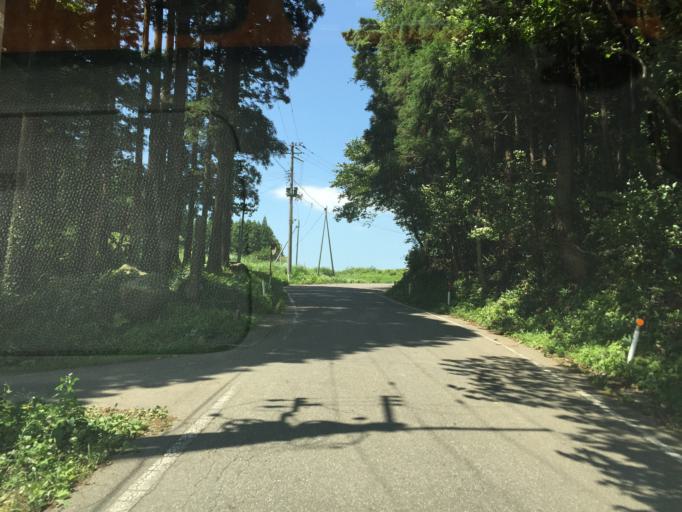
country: JP
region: Fukushima
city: Inawashiro
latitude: 37.5034
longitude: 140.0174
